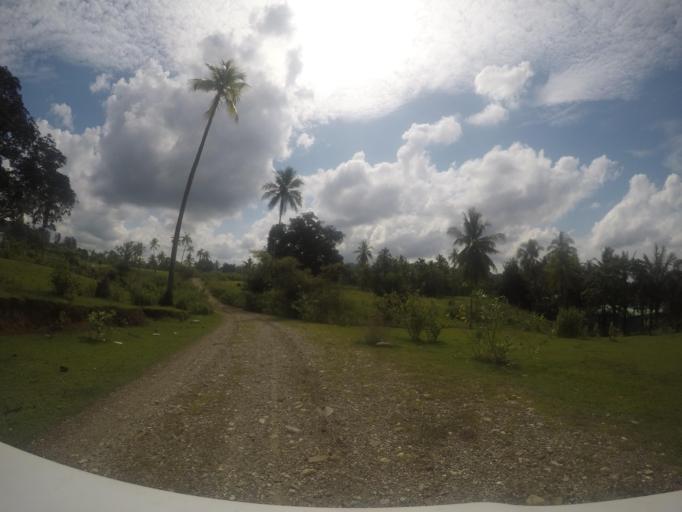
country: TL
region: Viqueque
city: Viqueque
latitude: -8.8496
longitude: 126.3632
